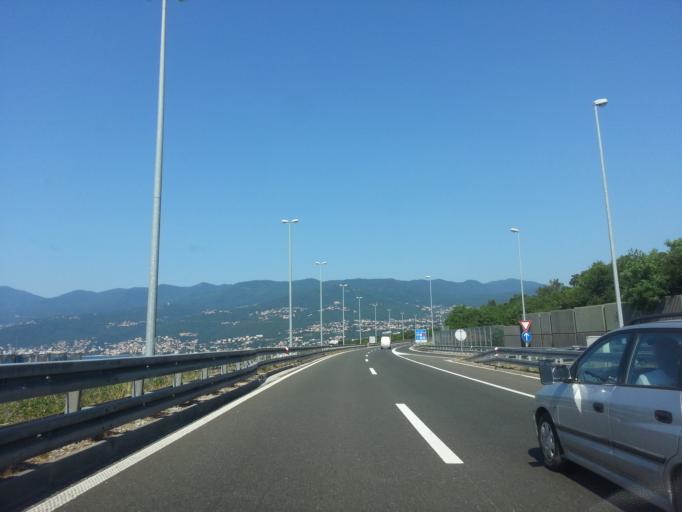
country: HR
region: Primorsko-Goranska
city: Rubesi
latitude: 45.3483
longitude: 14.3689
